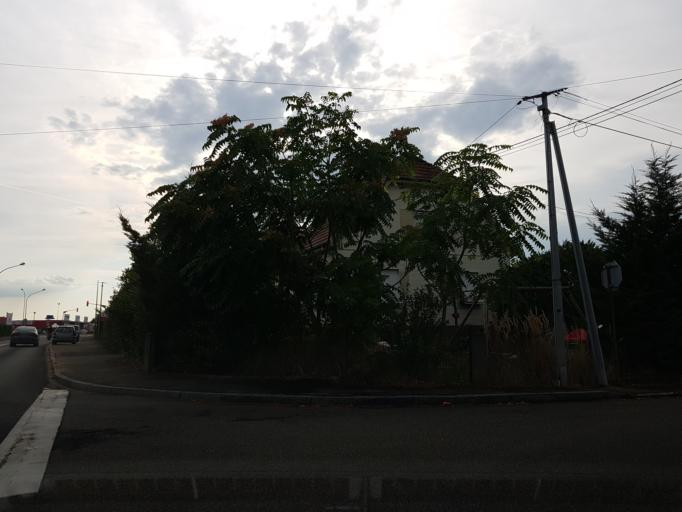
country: FR
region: Alsace
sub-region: Departement du Haut-Rhin
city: Kingersheim
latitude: 47.7991
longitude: 7.3150
